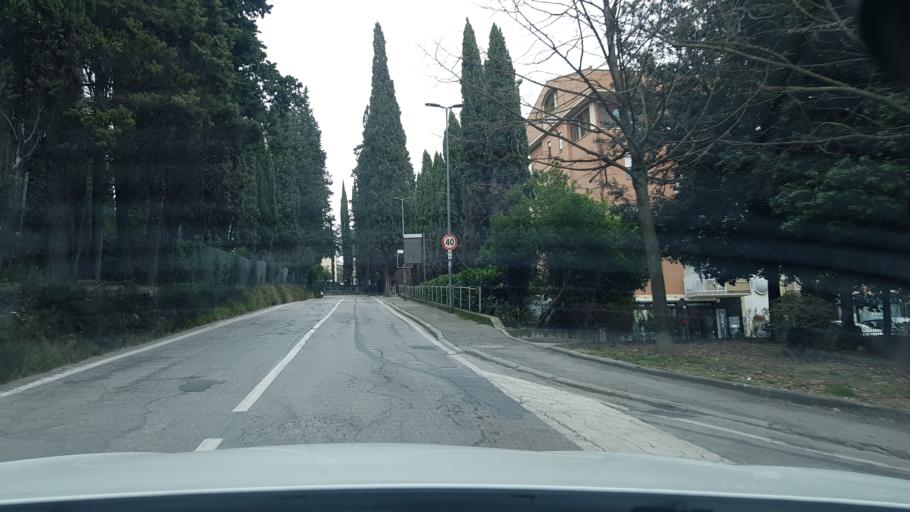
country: IT
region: Umbria
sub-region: Provincia di Perugia
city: Perugia
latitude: 43.1153
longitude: 12.3647
